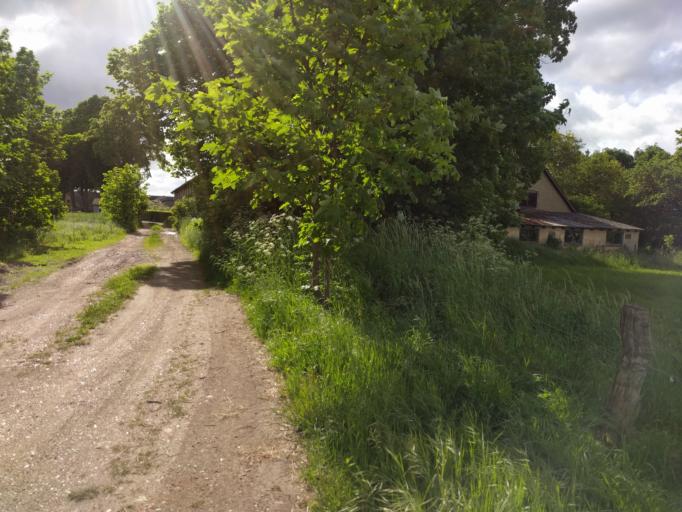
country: DK
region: South Denmark
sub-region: Nyborg Kommune
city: Ullerslev
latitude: 55.4013
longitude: 10.6155
